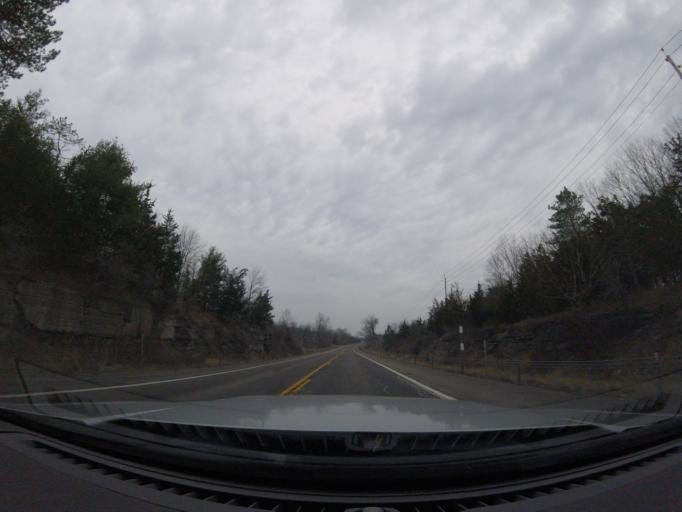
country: US
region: New York
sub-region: Yates County
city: Dundee
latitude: 42.5470
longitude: -76.9193
